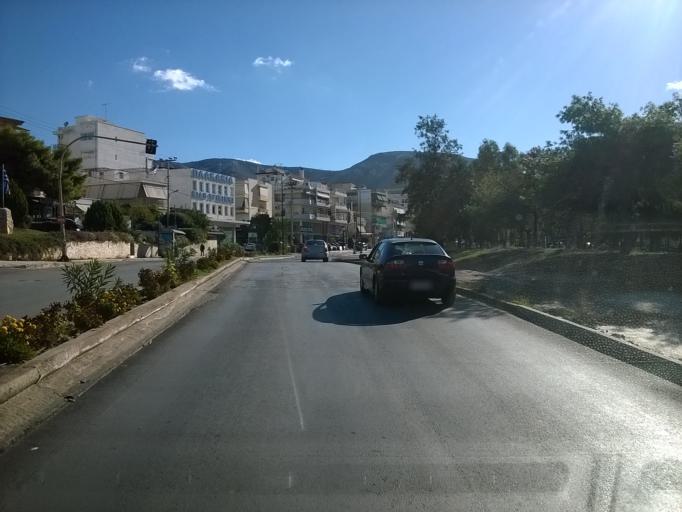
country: GR
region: Attica
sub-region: Nomarchia Athinas
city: Argyroupoli
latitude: 37.8960
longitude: 23.7602
